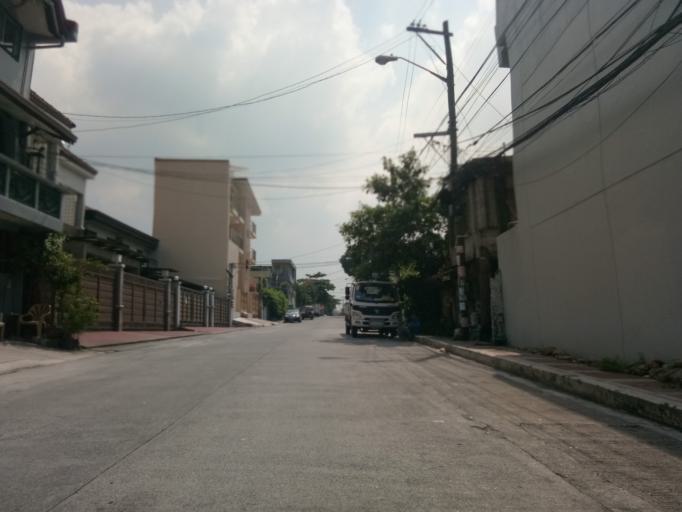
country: PH
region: Metro Manila
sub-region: Marikina
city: Calumpang
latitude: 14.6197
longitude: 121.0611
